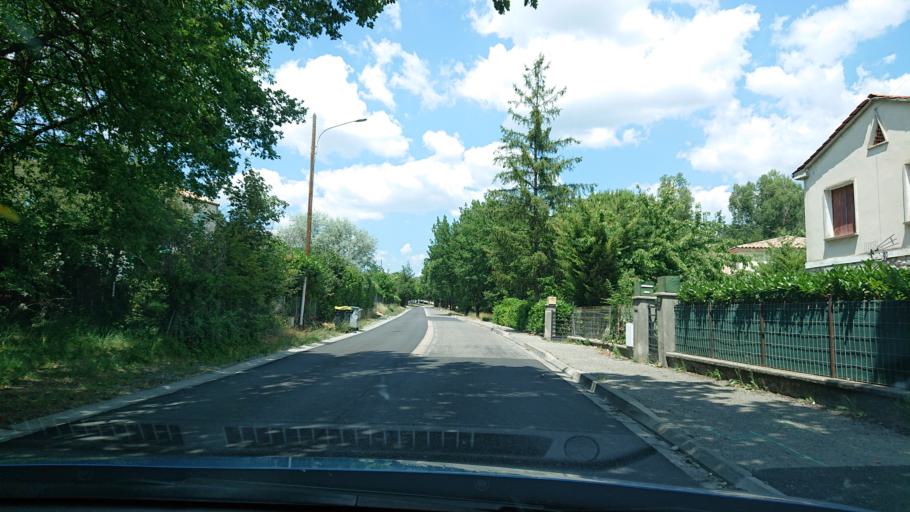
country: FR
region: Provence-Alpes-Cote d'Azur
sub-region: Departement des Alpes-de-Haute-Provence
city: Digne-les-Bains
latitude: 44.0778
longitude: 6.1755
